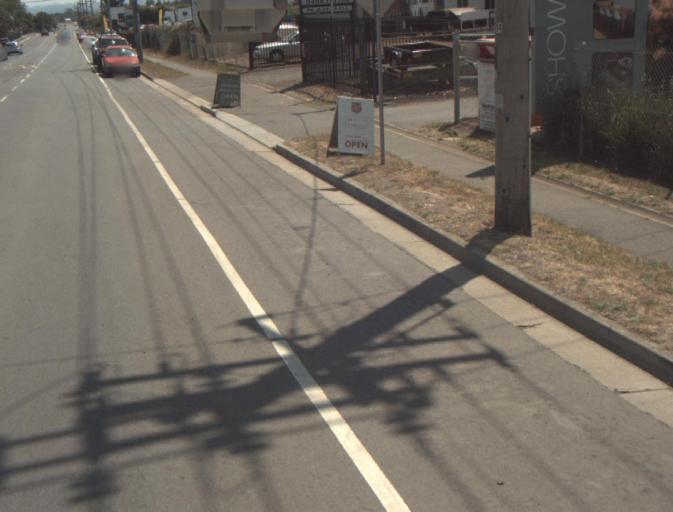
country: AU
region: Tasmania
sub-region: Launceston
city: Summerhill
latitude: -41.4891
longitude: 147.1679
